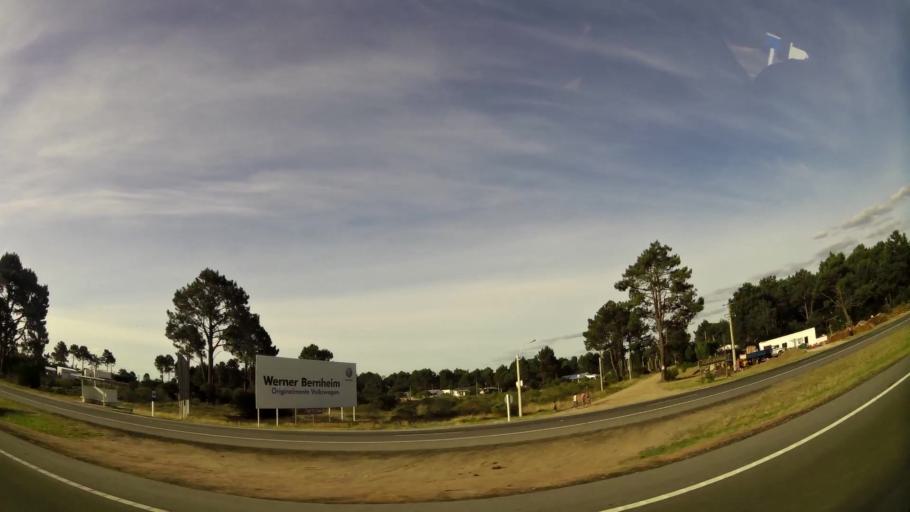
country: UY
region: Maldonado
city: Piriapolis
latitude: -34.7805
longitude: -55.4176
